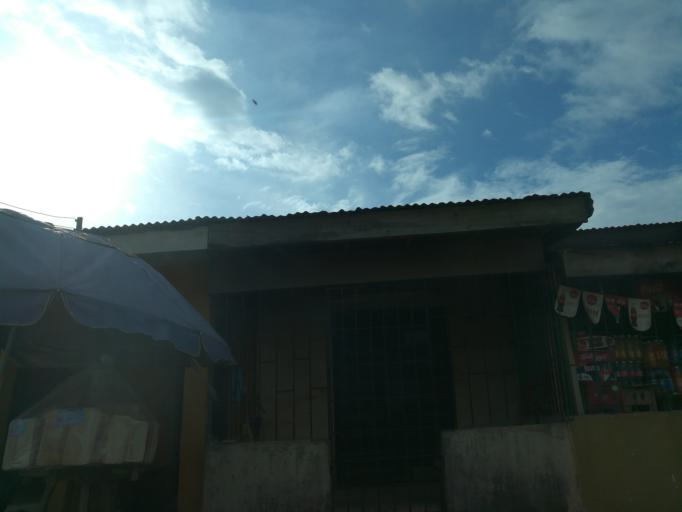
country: NG
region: Lagos
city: Ebute Ikorodu
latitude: 6.5989
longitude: 3.5007
